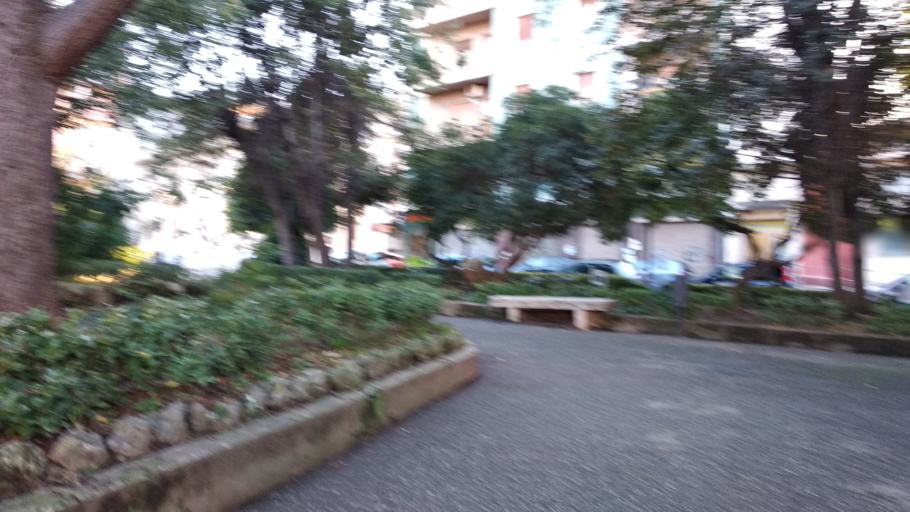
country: IT
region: Calabria
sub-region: Provincia di Reggio Calabria
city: Seminara
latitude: 38.3585
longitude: 15.8492
